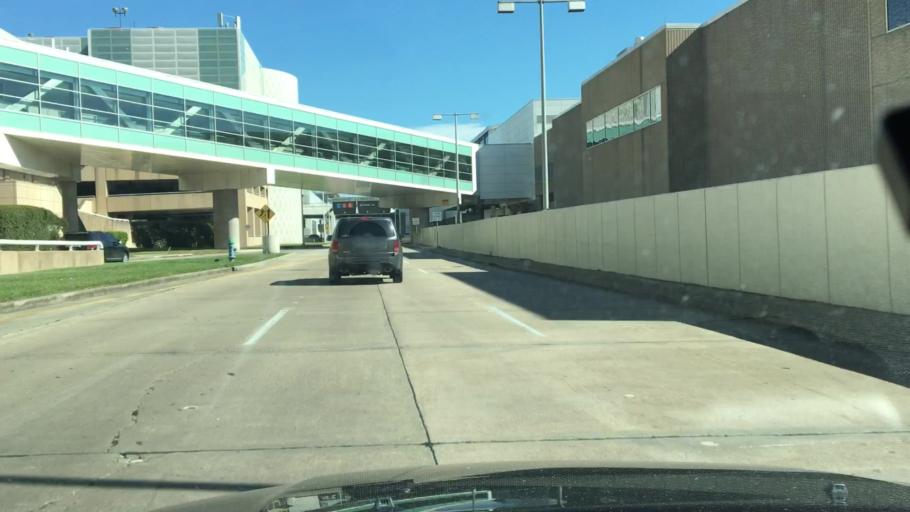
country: US
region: Texas
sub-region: Harris County
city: Aldine
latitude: 29.9860
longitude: -95.3367
